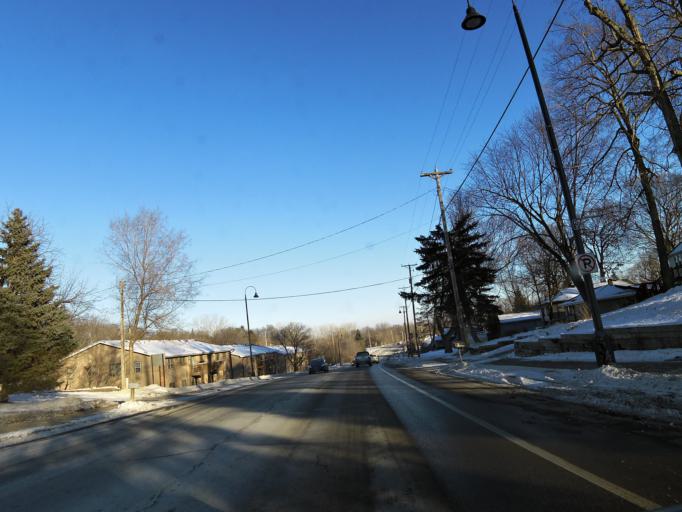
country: US
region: Minnesota
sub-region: Hennepin County
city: Mound
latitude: 44.9367
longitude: -93.6520
